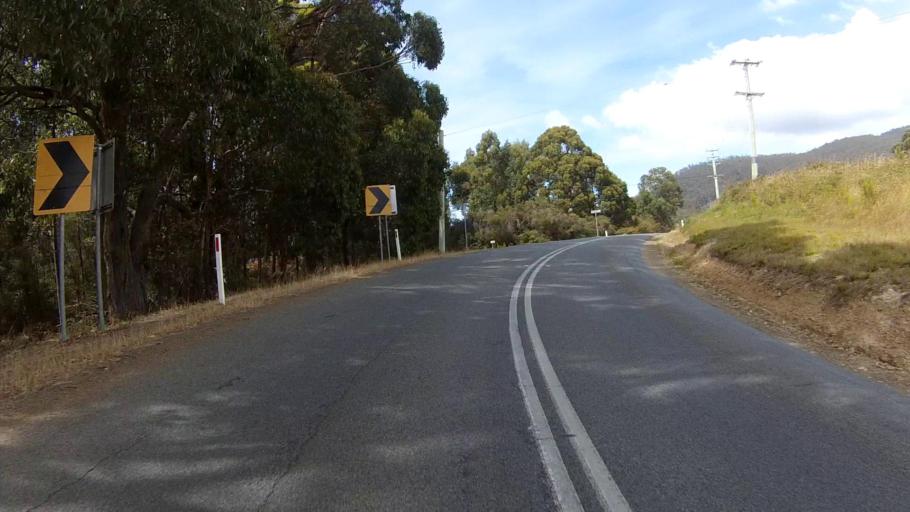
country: AU
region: Tasmania
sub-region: Kingborough
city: Kettering
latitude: -43.2113
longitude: 147.2565
